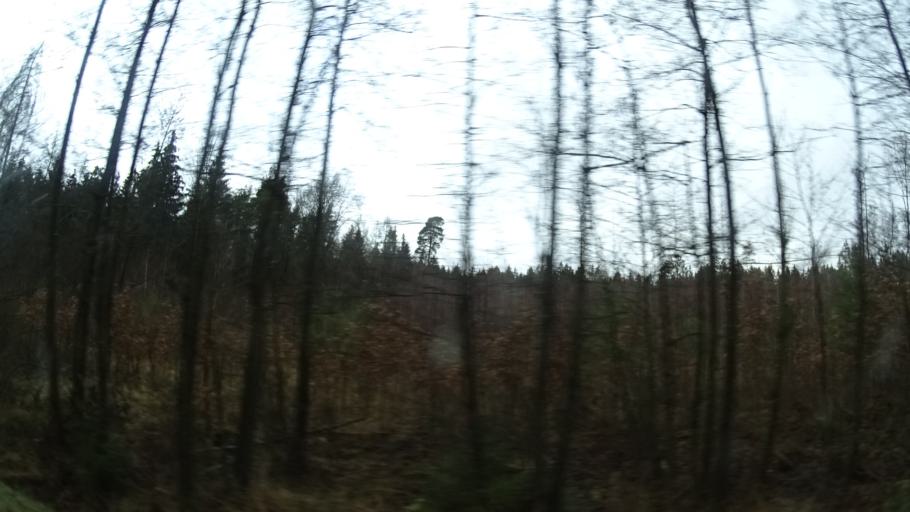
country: DE
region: Thuringia
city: Juchsen
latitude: 50.4625
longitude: 10.4727
